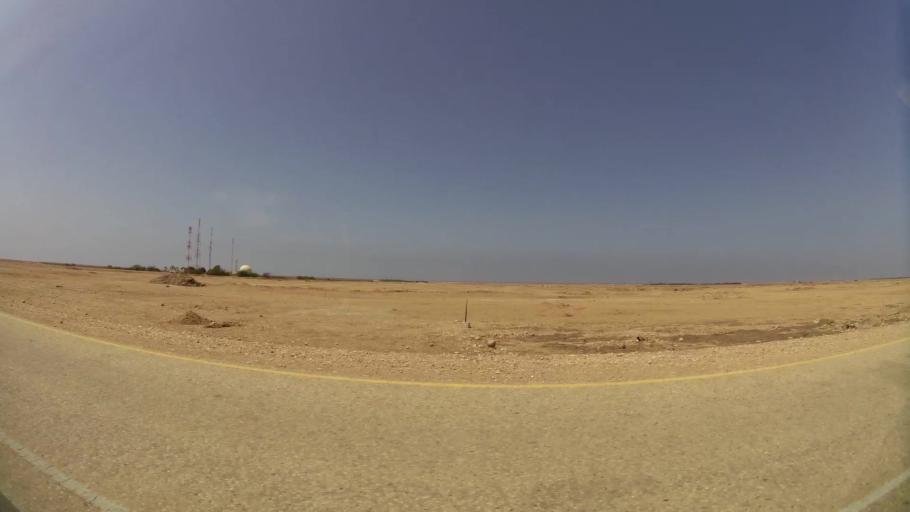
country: OM
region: Zufar
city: Salalah
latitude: 17.0368
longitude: 54.2570
